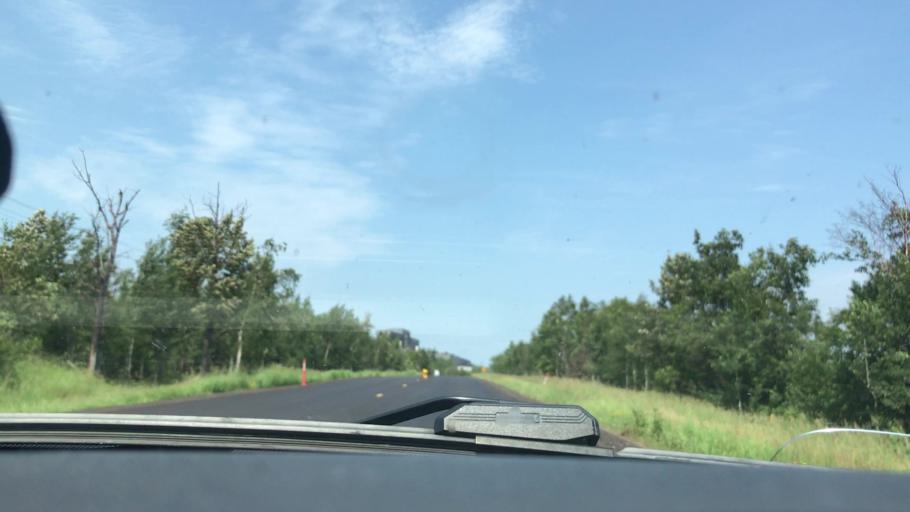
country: US
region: Minnesota
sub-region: Lake County
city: Silver Bay
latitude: 47.2837
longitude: -91.2682
